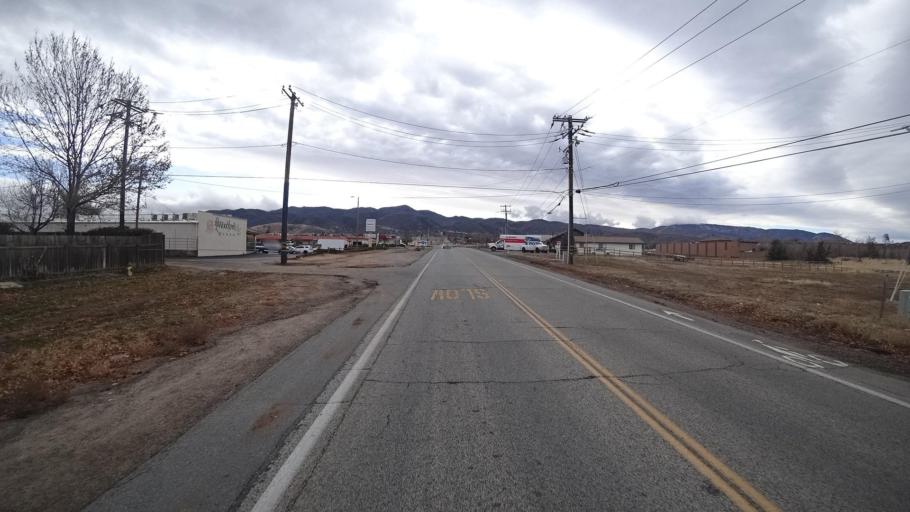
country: US
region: California
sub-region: Kern County
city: Golden Hills
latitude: 35.1260
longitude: -118.4948
